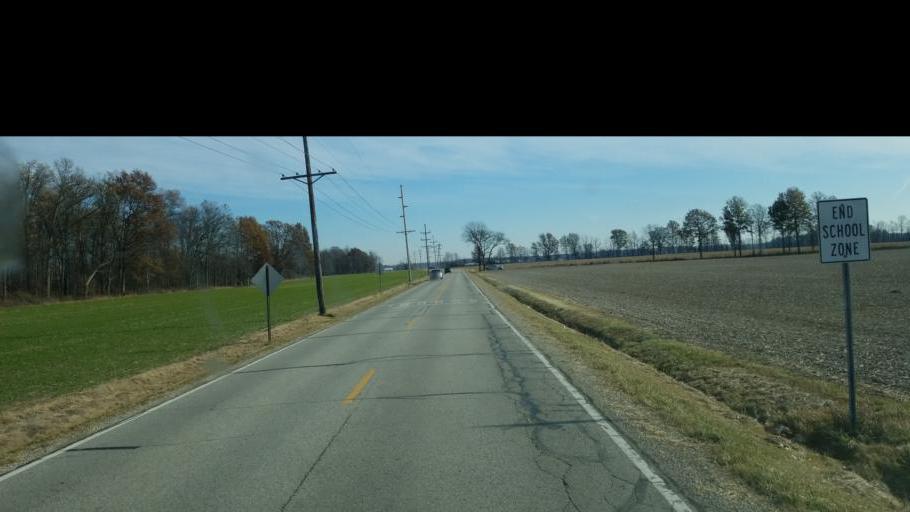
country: US
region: Ohio
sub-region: Crawford County
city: Galion
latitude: 40.7842
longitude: -82.8547
